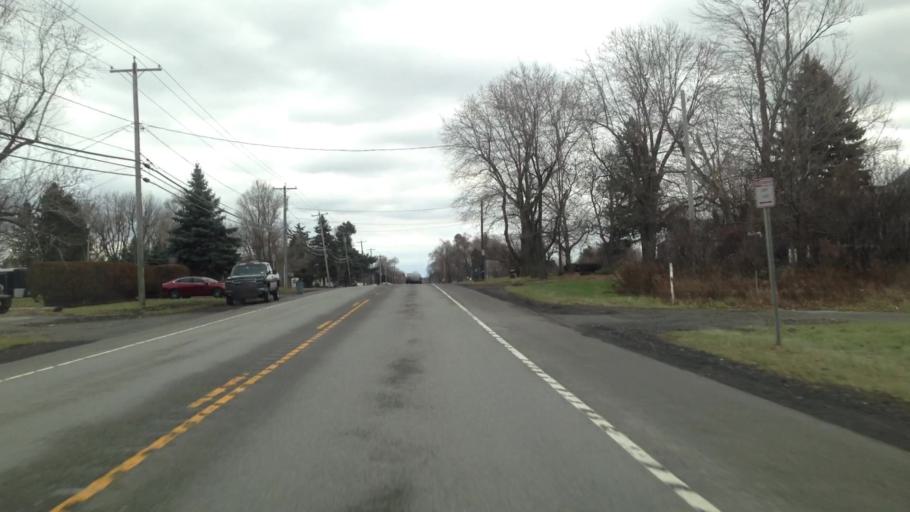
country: US
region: New York
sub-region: Erie County
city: Clarence
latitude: 42.9863
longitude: -78.5657
